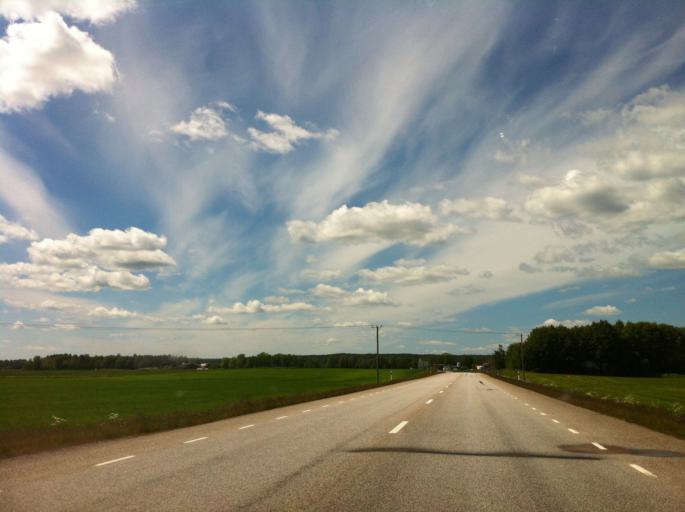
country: SE
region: Vaestra Goetaland
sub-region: Amals Kommun
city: Amal
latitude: 58.9802
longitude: 12.6423
